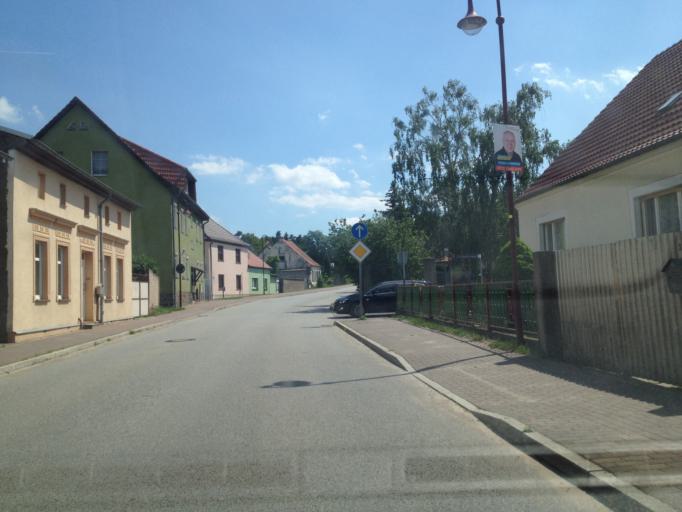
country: DE
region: Brandenburg
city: Joachimsthal
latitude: 52.9757
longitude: 13.7540
